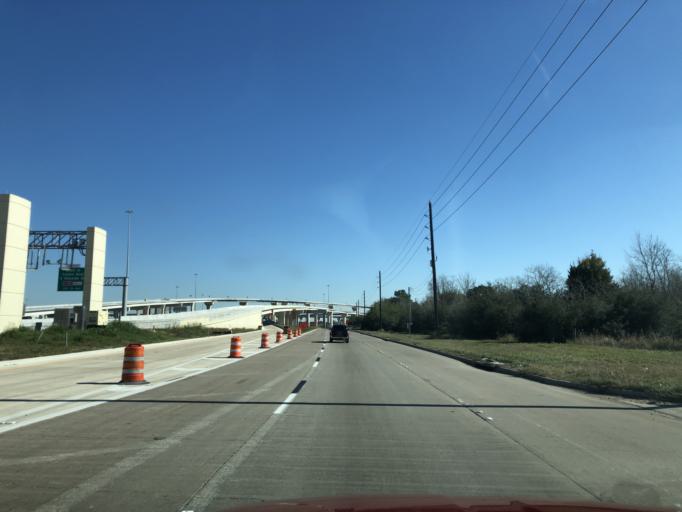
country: US
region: Texas
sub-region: Brazoria County
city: Brookside Village
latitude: 29.5966
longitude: -95.3952
